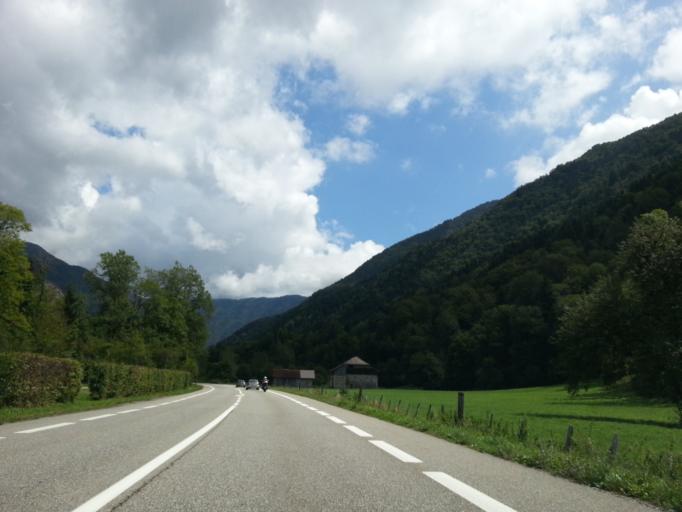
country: FR
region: Rhone-Alpes
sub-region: Departement de la Haute-Savoie
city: Dingy-Saint-Clair
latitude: 45.8917
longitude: 6.2551
